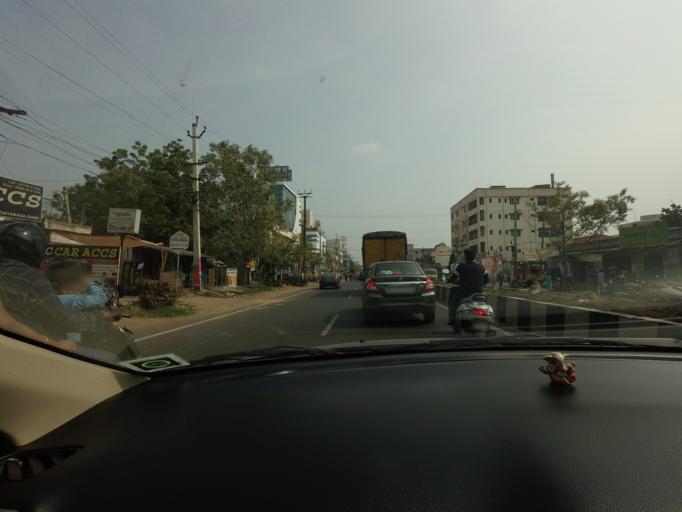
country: IN
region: Andhra Pradesh
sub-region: Krishna
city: Yanamalakuduru
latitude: 16.4878
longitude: 80.6770
